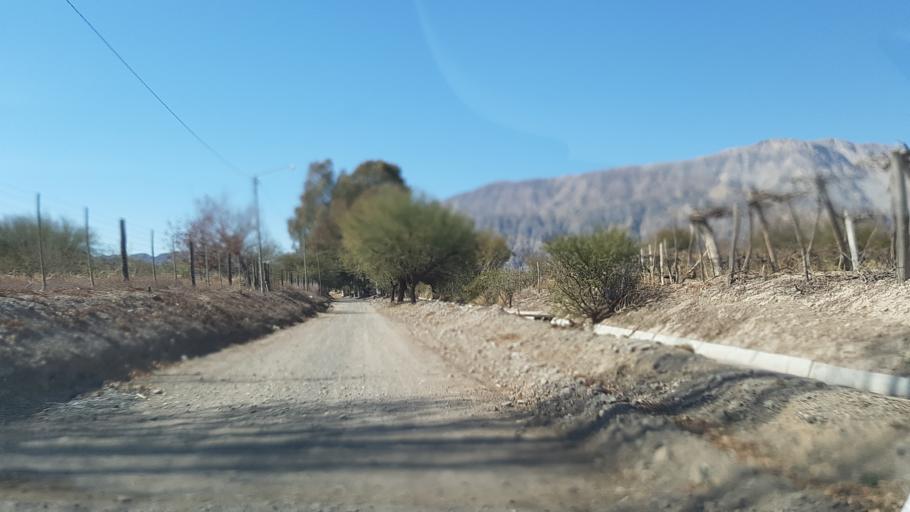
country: AR
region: San Juan
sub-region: Departamento de Zonda
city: Zonda
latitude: -31.5707
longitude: -68.7433
